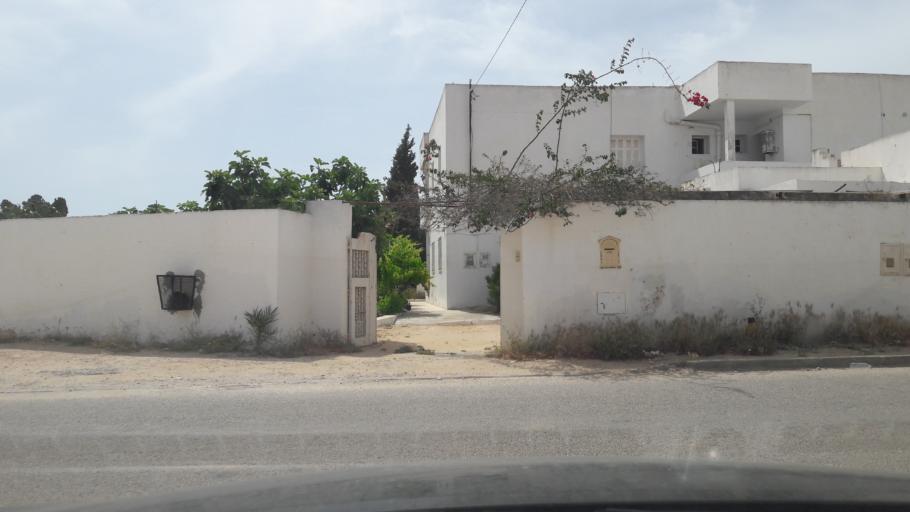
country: TN
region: Safaqis
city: Sfax
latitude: 34.7846
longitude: 10.7545
